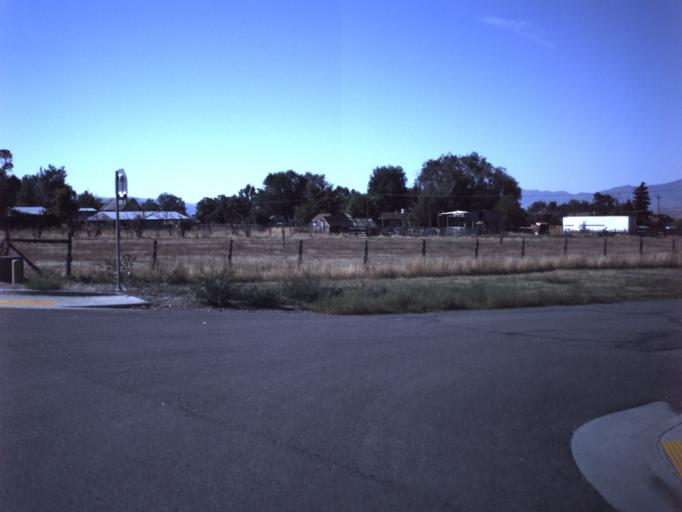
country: US
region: Utah
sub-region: Juab County
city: Nephi
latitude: 39.5560
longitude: -111.8639
